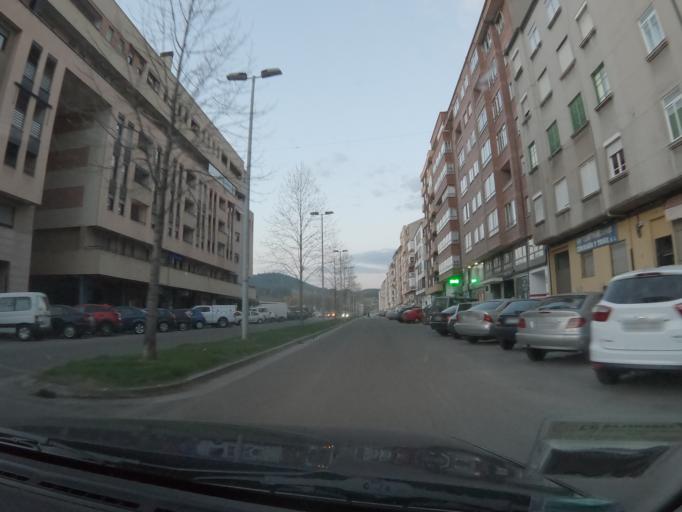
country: ES
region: Castille and Leon
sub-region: Provincia de Leon
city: Ponferrada
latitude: 42.5492
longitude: -6.5898
